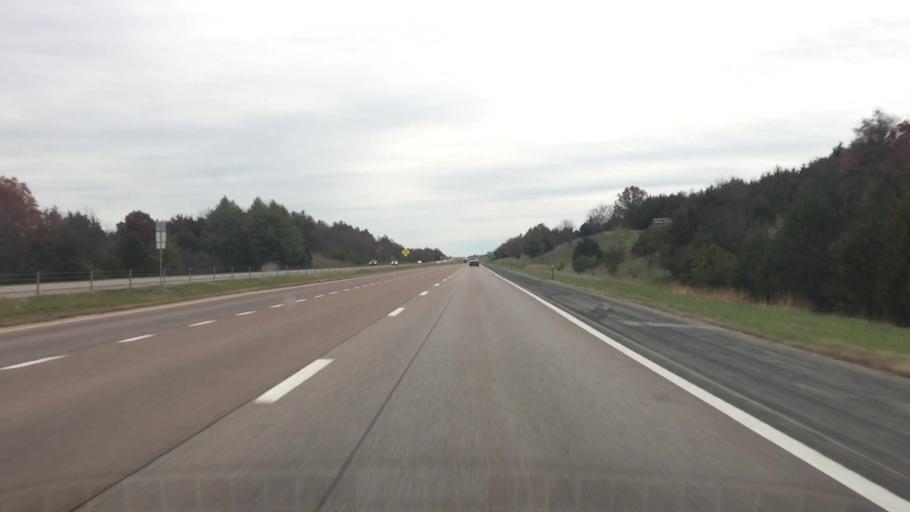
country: US
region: Missouri
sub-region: Boone County
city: Ashland
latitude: 38.7521
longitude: -92.2530
